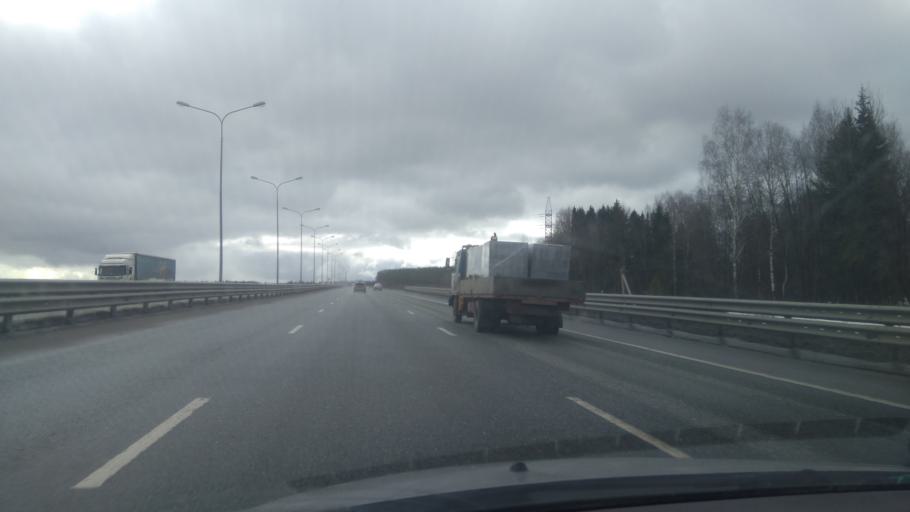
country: RU
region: Perm
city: Bershet'
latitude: 57.7170
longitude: 56.3593
